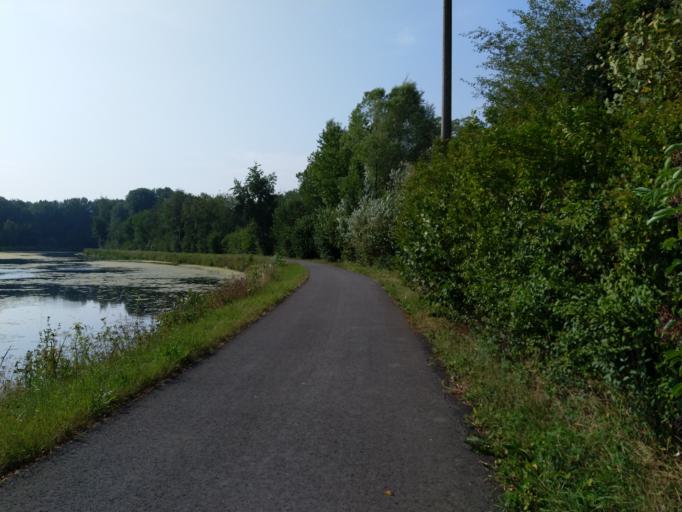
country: BE
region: Wallonia
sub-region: Province du Hainaut
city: Seneffe
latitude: 50.5766
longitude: 4.2522
